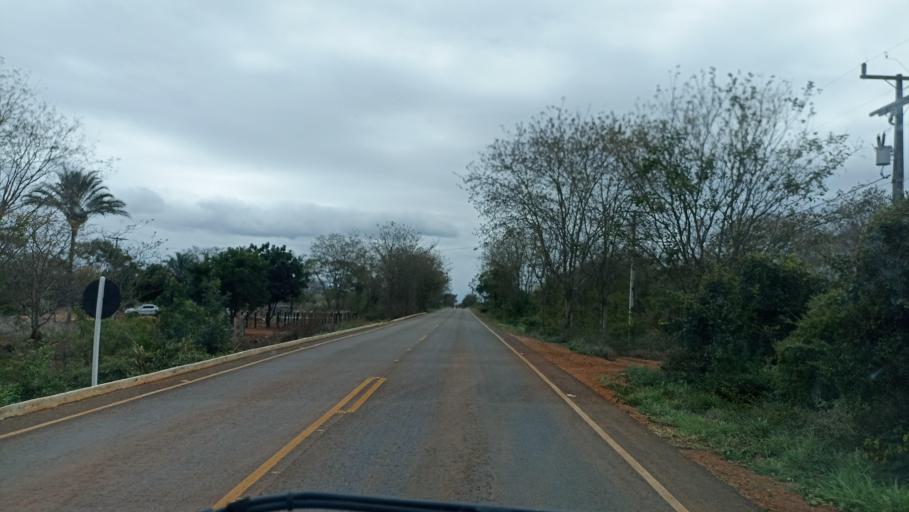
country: BR
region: Bahia
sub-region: Andarai
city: Vera Cruz
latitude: -12.9784
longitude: -41.0178
